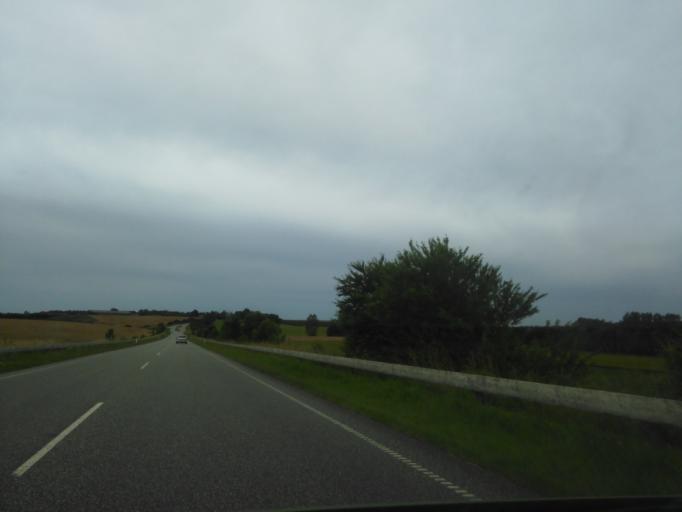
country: DK
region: Central Jutland
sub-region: Horsens Kommune
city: Horsens
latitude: 55.9002
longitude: 9.8811
